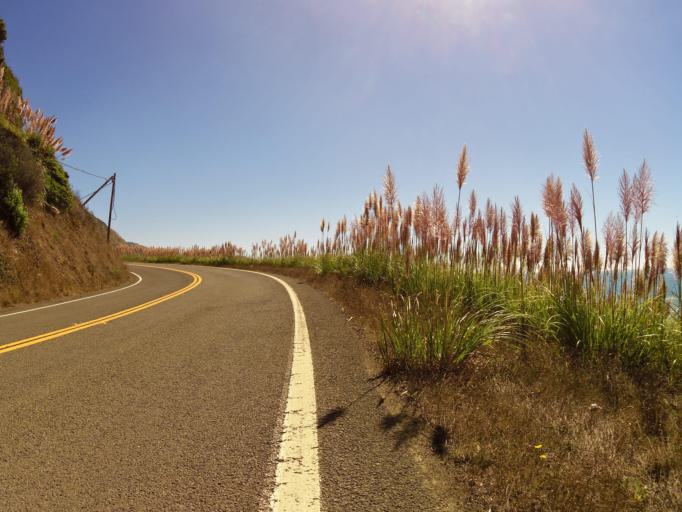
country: US
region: California
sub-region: Mendocino County
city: Fort Bragg
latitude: 39.6977
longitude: -123.8001
